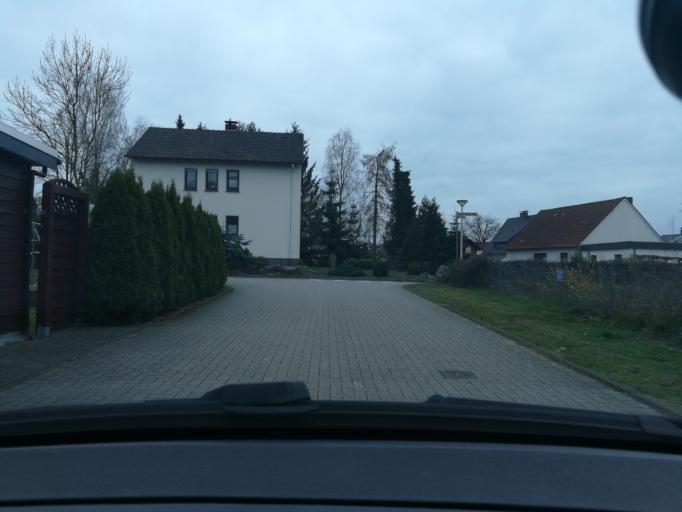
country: DE
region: North Rhine-Westphalia
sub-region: Regierungsbezirk Detmold
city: Oerlinghausen
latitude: 51.9378
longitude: 8.6343
